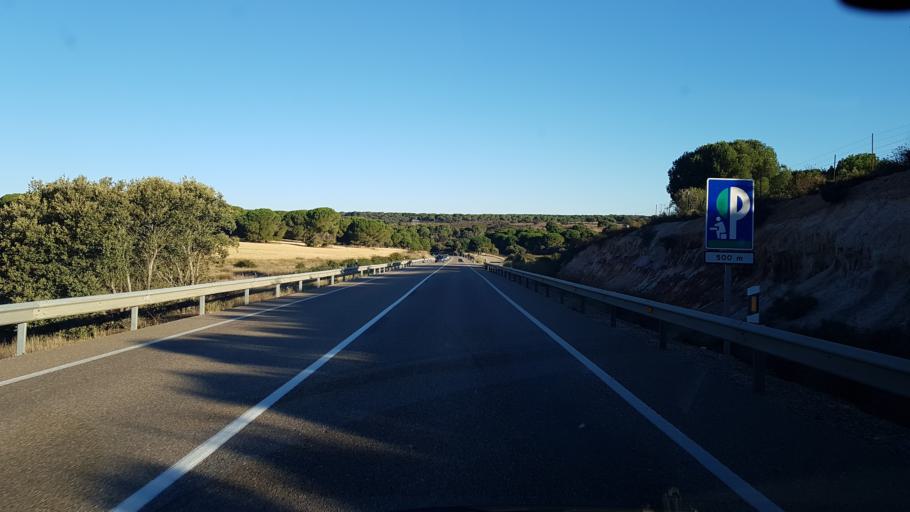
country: ES
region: Castille and Leon
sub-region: Provincia de Zamora
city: Roales
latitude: 41.5310
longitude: -5.8219
